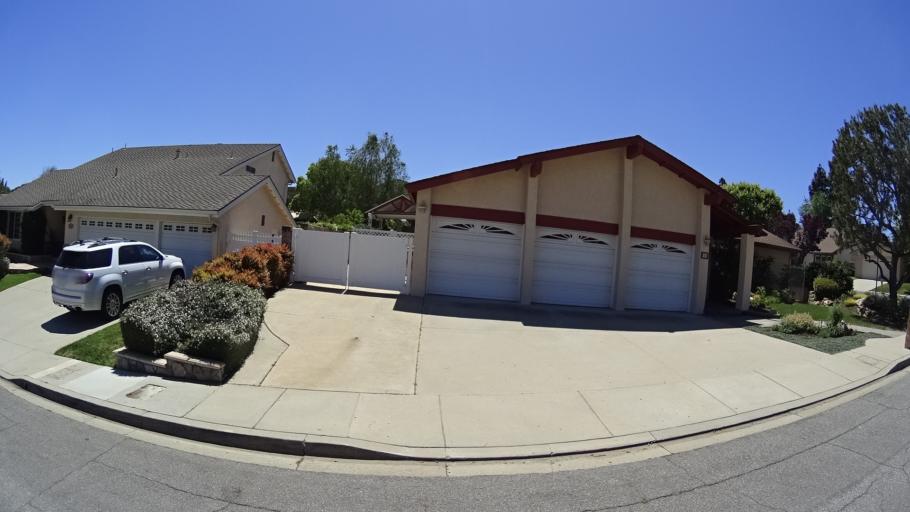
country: US
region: California
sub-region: Ventura County
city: Casa Conejo
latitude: 34.1785
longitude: -118.8998
